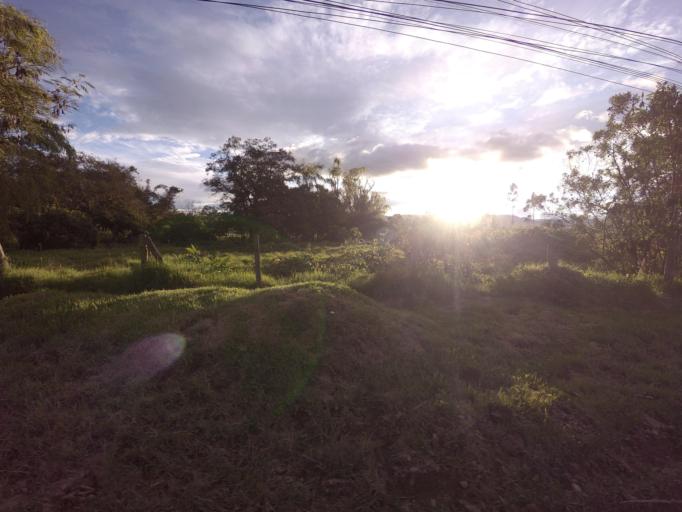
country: CO
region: Cundinamarca
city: Chia
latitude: 4.8105
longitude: -74.0307
